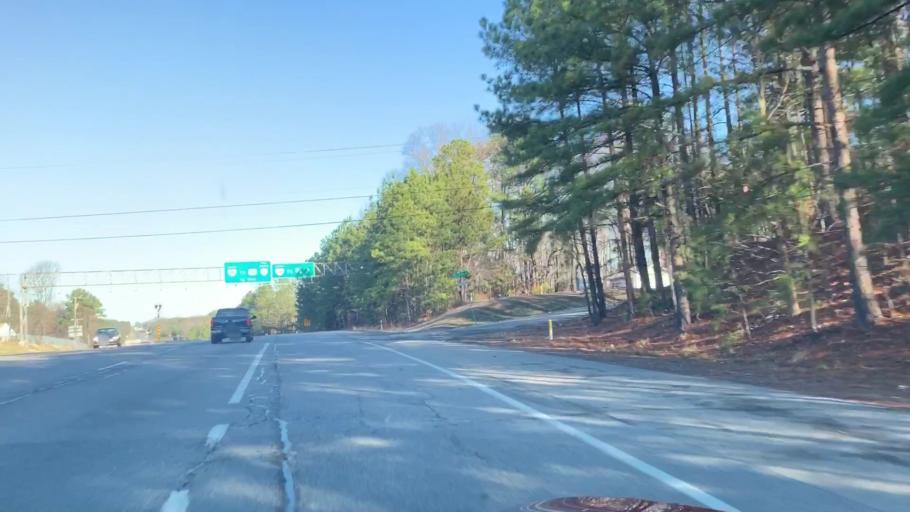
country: US
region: Virginia
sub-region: Chesterfield County
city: Chester
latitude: 37.3725
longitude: -77.4184
